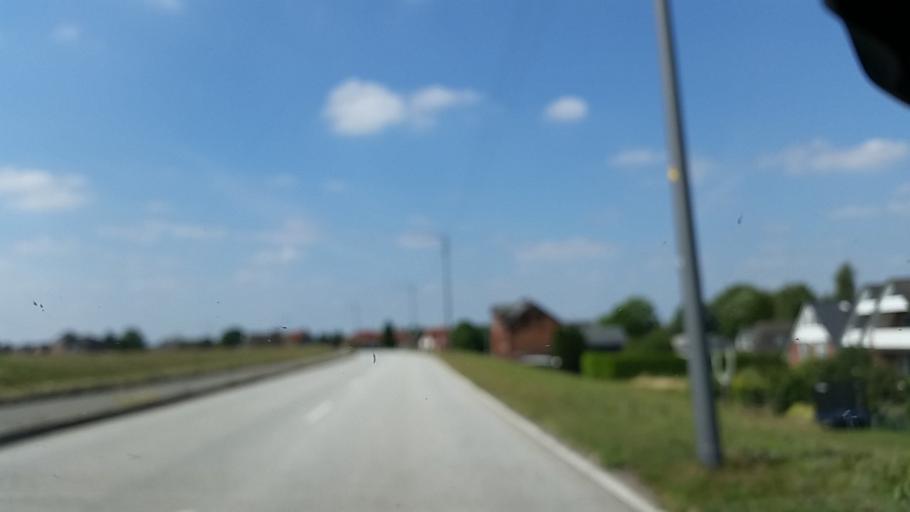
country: DE
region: Lower Saxony
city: Winsen
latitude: 53.4035
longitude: 10.1979
